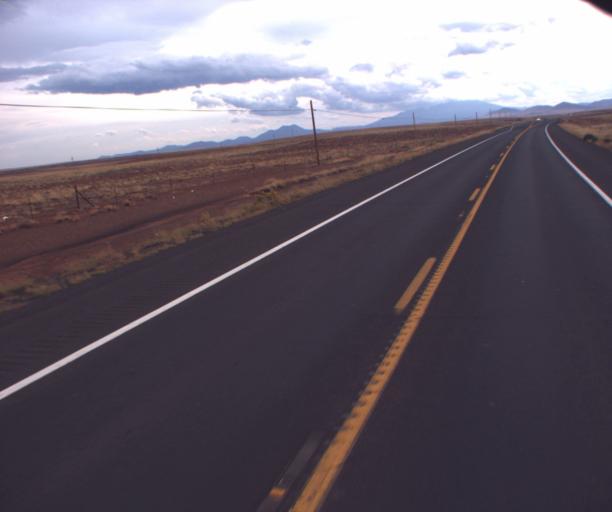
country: US
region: Arizona
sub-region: Coconino County
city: Tuba City
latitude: 35.7196
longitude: -111.4858
